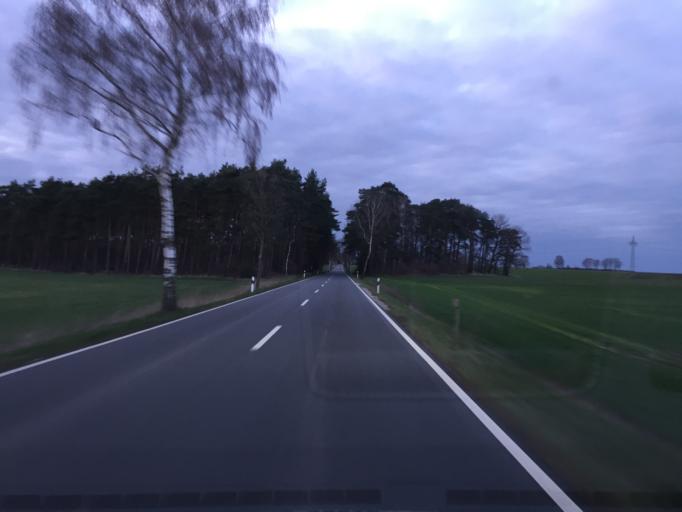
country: DE
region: Lower Saxony
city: Steimbke
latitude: 52.6078
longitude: 9.3932
